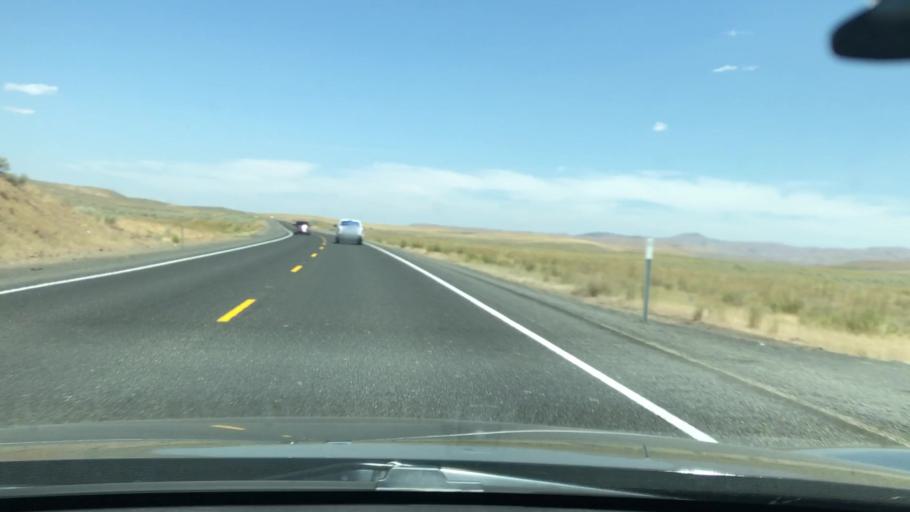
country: US
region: Idaho
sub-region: Owyhee County
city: Marsing
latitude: 43.1315
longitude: -117.0482
